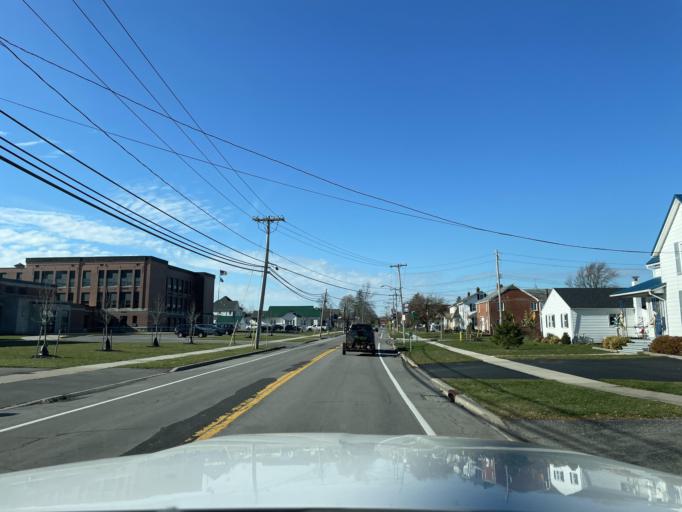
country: US
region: New York
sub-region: Niagara County
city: Middleport
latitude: 43.2128
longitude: -78.4678
